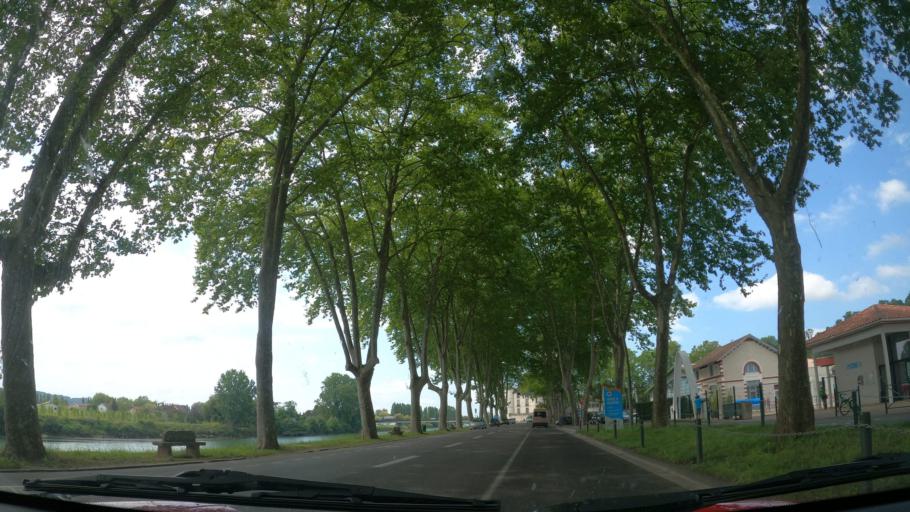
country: FR
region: Aquitaine
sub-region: Departement des Landes
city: Peyrehorade
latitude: 43.5433
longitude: -1.1017
